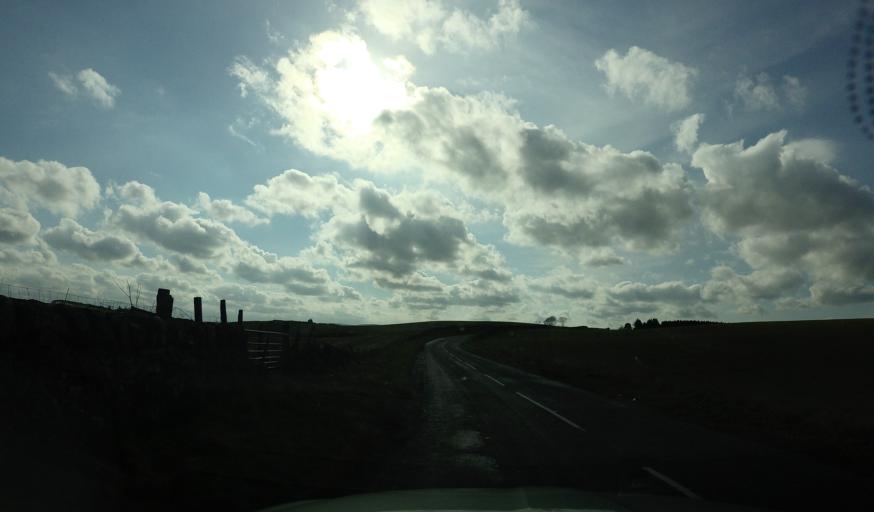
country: GB
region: Scotland
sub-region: Midlothian
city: Penicuik
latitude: 55.8104
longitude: -3.1847
